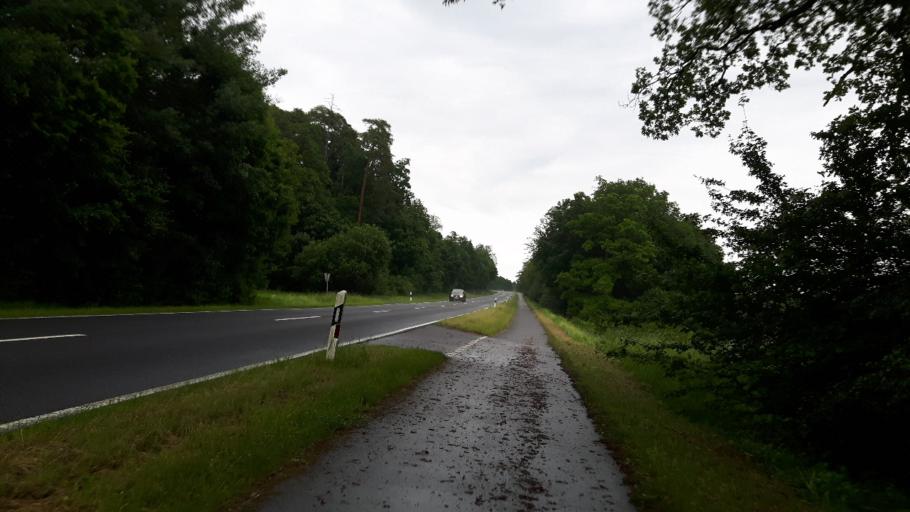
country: DE
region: Bavaria
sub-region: Regierungsbezirk Unterfranken
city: Uchtelhausen
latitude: 50.1231
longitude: 10.2819
